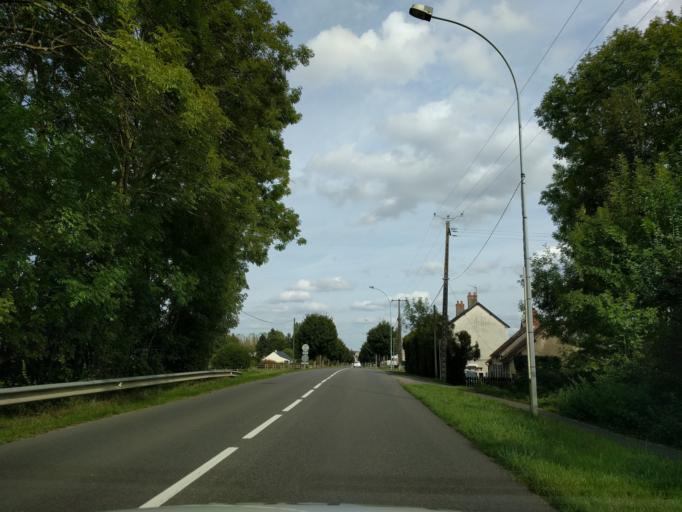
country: FR
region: Bourgogne
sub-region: Departement de la Nievre
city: La Charite-sur-Loire
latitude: 47.1700
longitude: 2.9964
